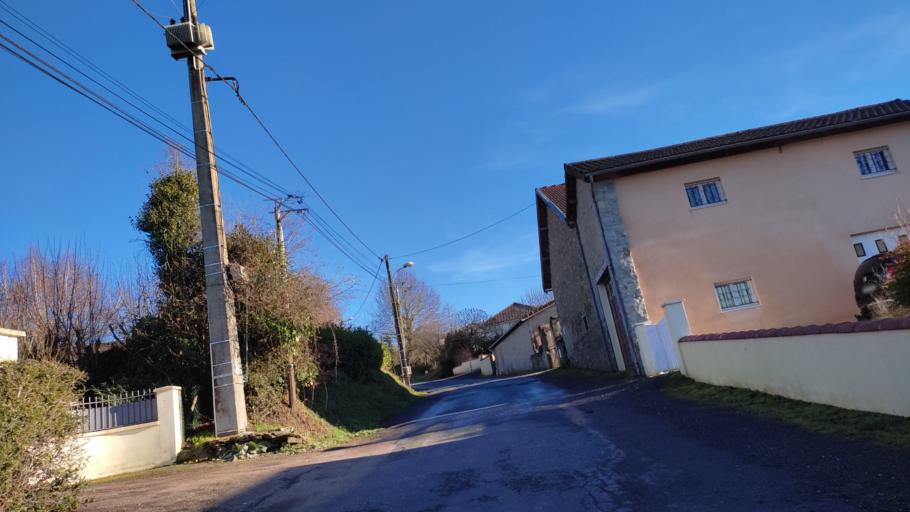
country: FR
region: Limousin
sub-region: Departement de la Haute-Vienne
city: Isle
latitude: 45.8092
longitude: 1.1977
